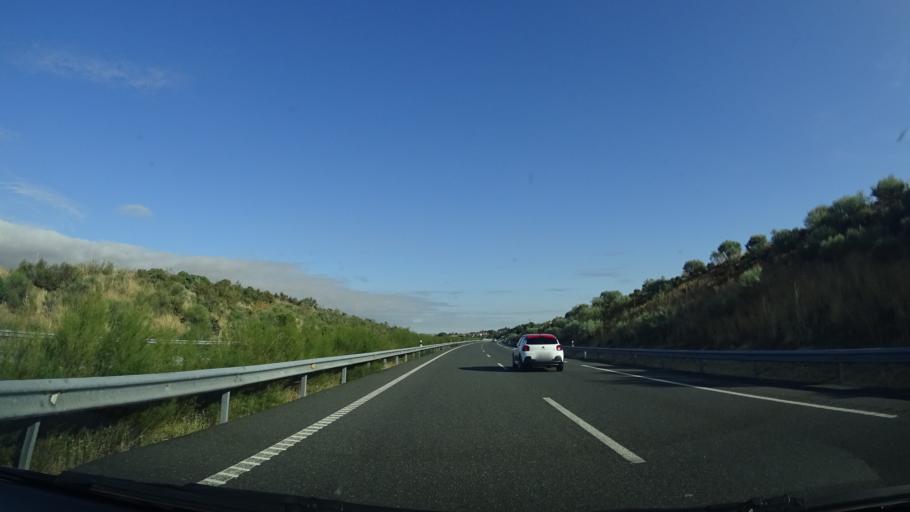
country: ES
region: Castille and Leon
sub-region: Provincia de Segovia
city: Labajos
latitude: 40.8481
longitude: -4.5424
